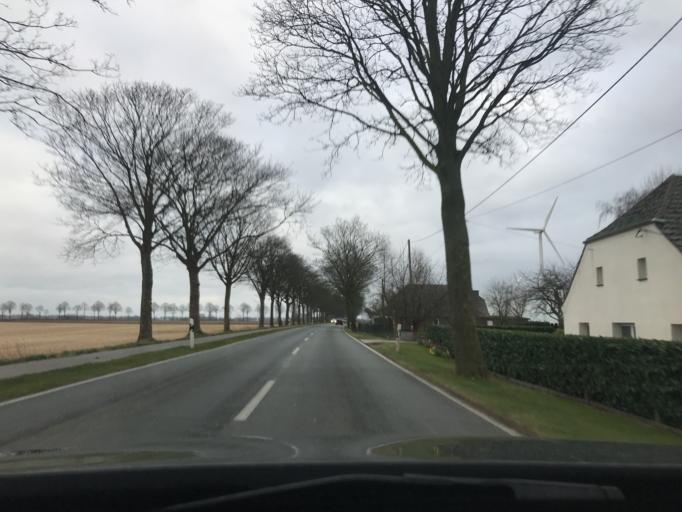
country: DE
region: North Rhine-Westphalia
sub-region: Regierungsbezirk Dusseldorf
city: Goch
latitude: 51.7242
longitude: 6.2144
